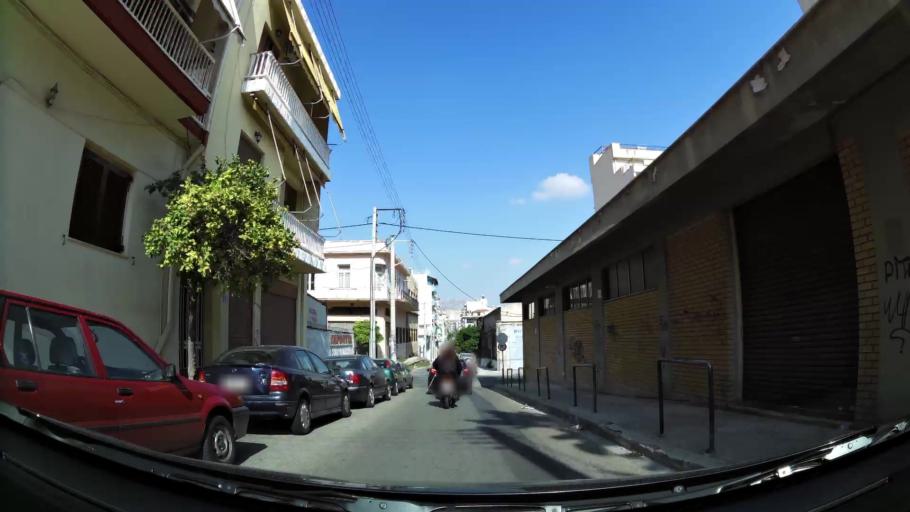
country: GR
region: Attica
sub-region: Nomos Attikis
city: Piraeus
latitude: 37.9511
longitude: 23.6325
